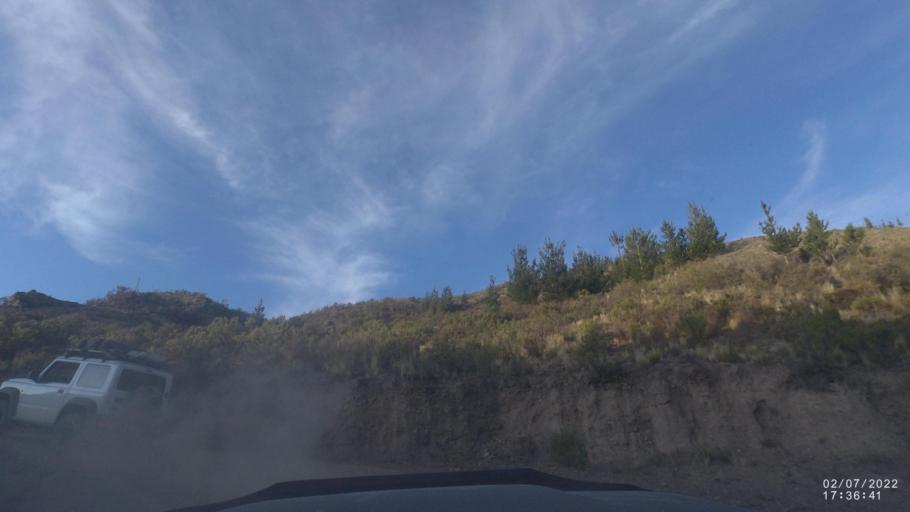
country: BO
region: Cochabamba
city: Irpa Irpa
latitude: -17.8752
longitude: -66.6192
